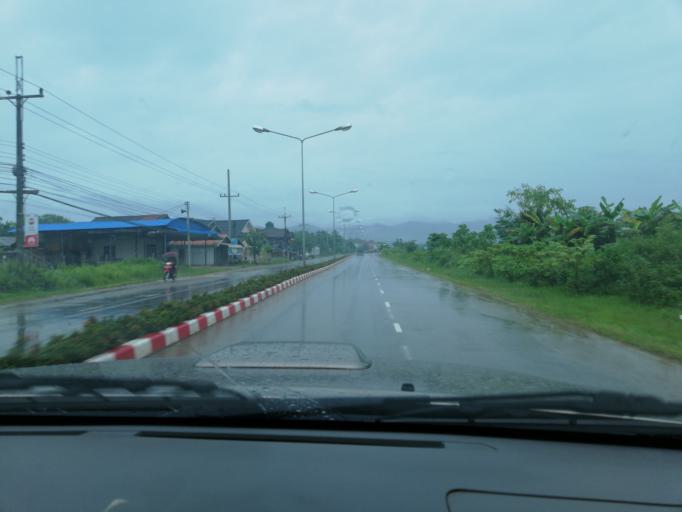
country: LA
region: Loungnamtha
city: Louang Namtha
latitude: 20.9577
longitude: 101.4041
